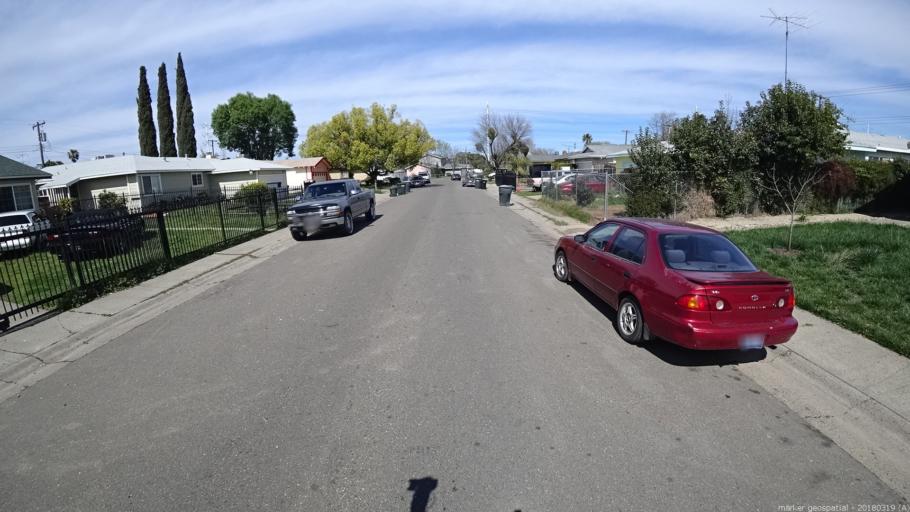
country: US
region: California
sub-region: Sacramento County
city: Parkway
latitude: 38.5067
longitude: -121.4376
